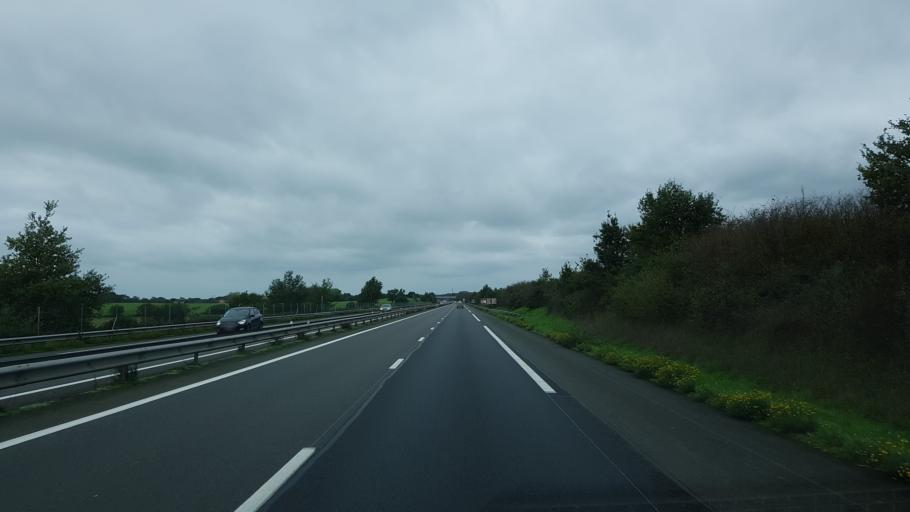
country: FR
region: Pays de la Loire
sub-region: Departement de la Loire-Atlantique
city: Le Bignon
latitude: 47.0926
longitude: -1.4622
